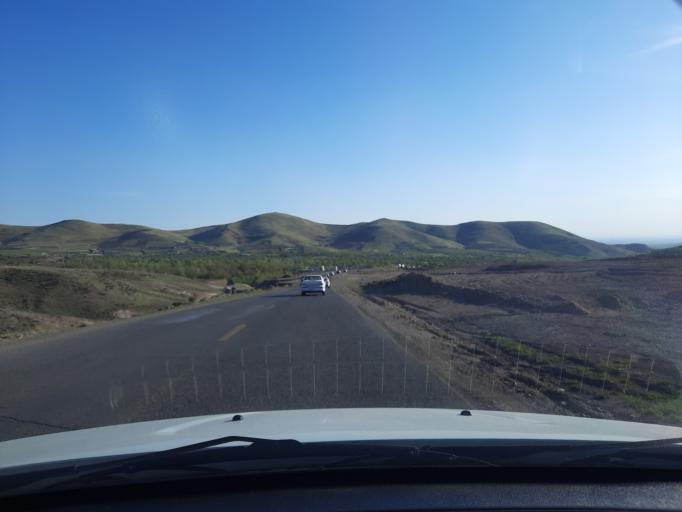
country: IR
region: Qazvin
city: Qazvin
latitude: 36.3508
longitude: 50.1872
